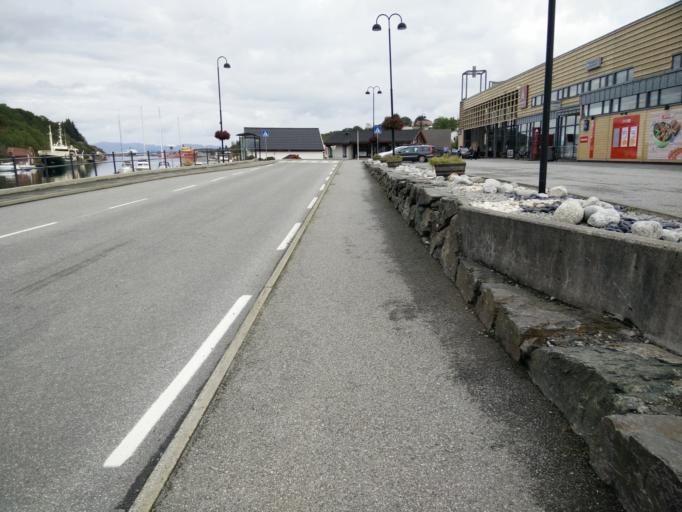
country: NO
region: Hordaland
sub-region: Sveio
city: Sveio
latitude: 59.6019
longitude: 5.2088
